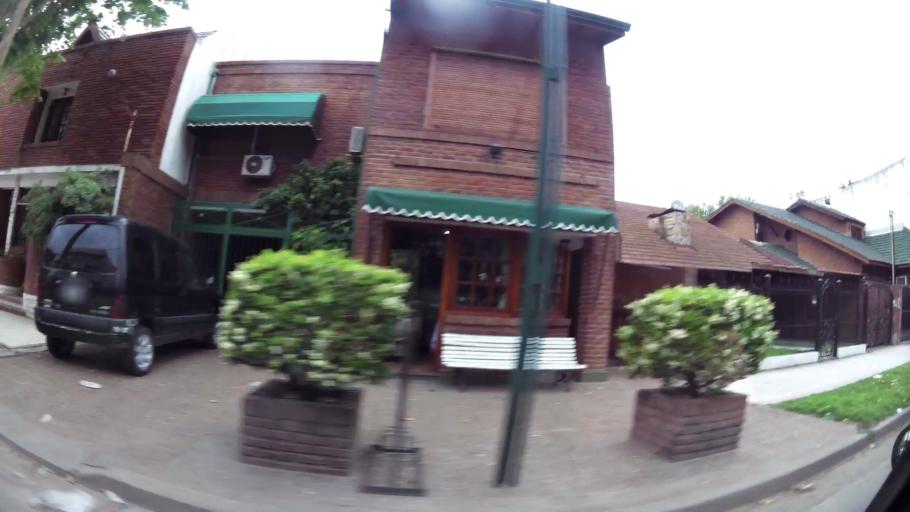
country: AR
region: Buenos Aires
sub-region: Partido de Quilmes
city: Quilmes
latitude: -34.8043
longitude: -58.2748
